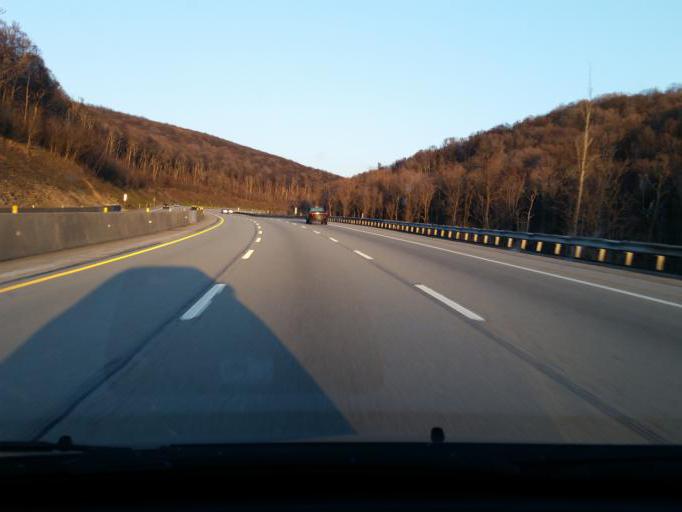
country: US
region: Pennsylvania
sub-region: Westmoreland County
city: Ligonier
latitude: 40.1138
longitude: -79.2552
